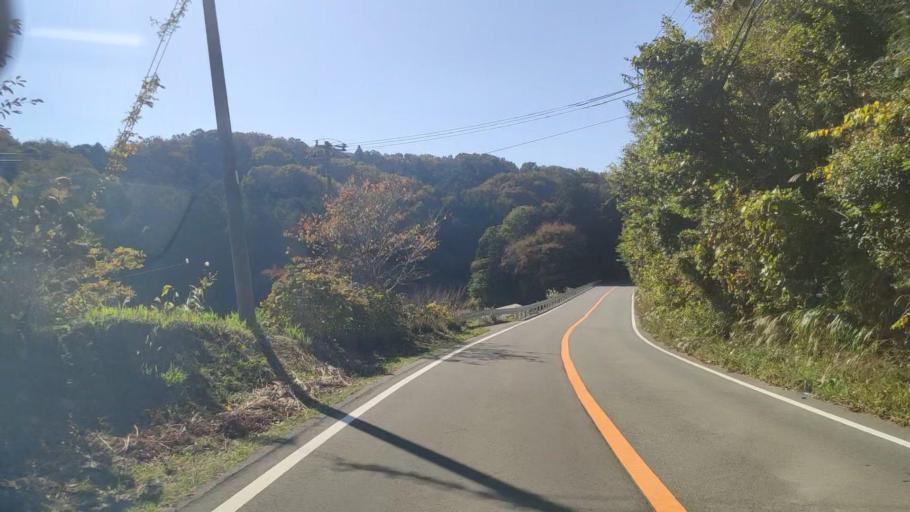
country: JP
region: Shizuoka
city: Atami
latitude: 35.0230
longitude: 139.0123
